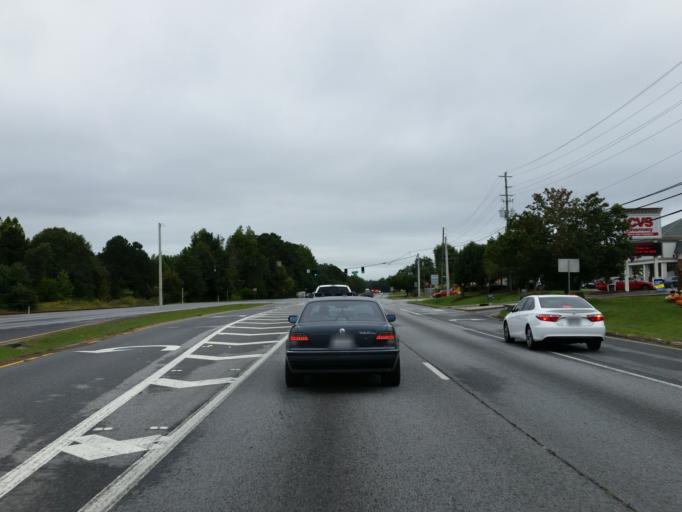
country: US
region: Georgia
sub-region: Clayton County
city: Bonanza
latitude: 33.4749
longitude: -84.3373
